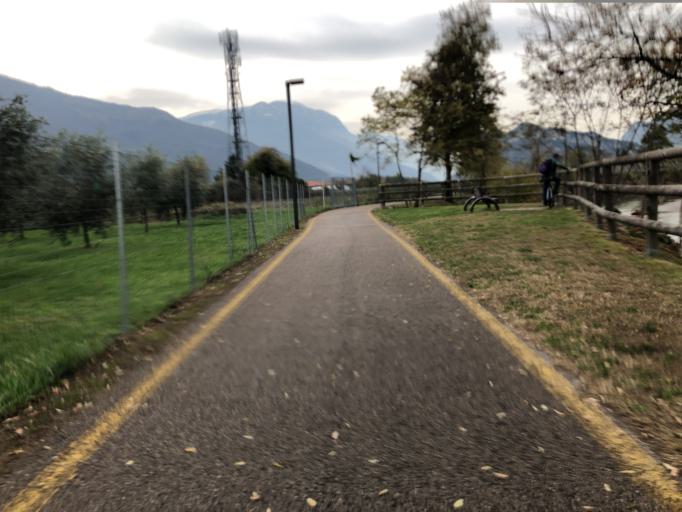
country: IT
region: Trentino-Alto Adige
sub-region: Provincia di Trento
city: Arco
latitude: 45.9153
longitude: 10.8890
